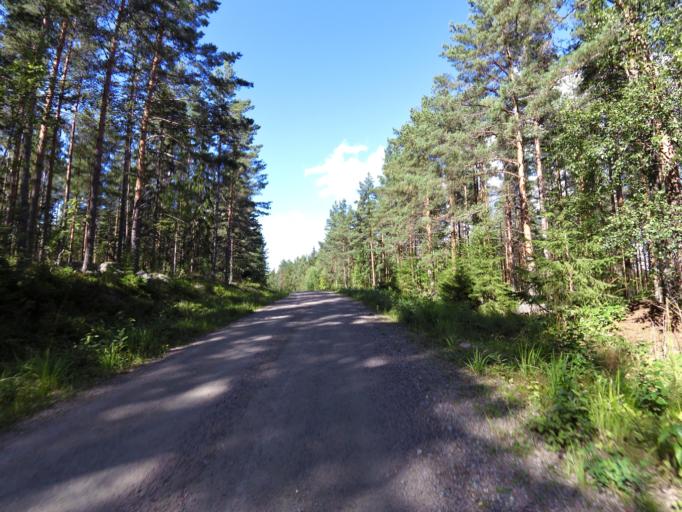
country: SE
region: Gaevleborg
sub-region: Gavle Kommun
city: Valbo
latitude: 60.7846
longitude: 16.9028
